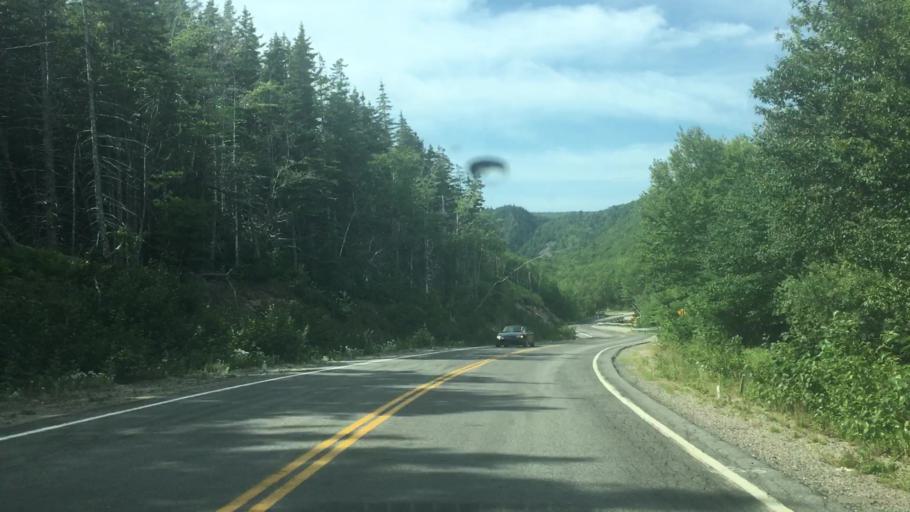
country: CA
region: Nova Scotia
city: Sydney Mines
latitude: 46.5822
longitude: -60.3936
